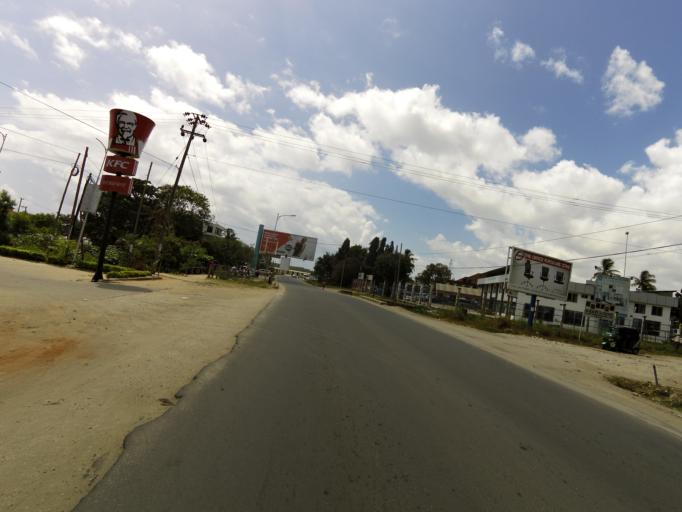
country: TZ
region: Dar es Salaam
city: Magomeni
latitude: -6.7636
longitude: 39.2566
